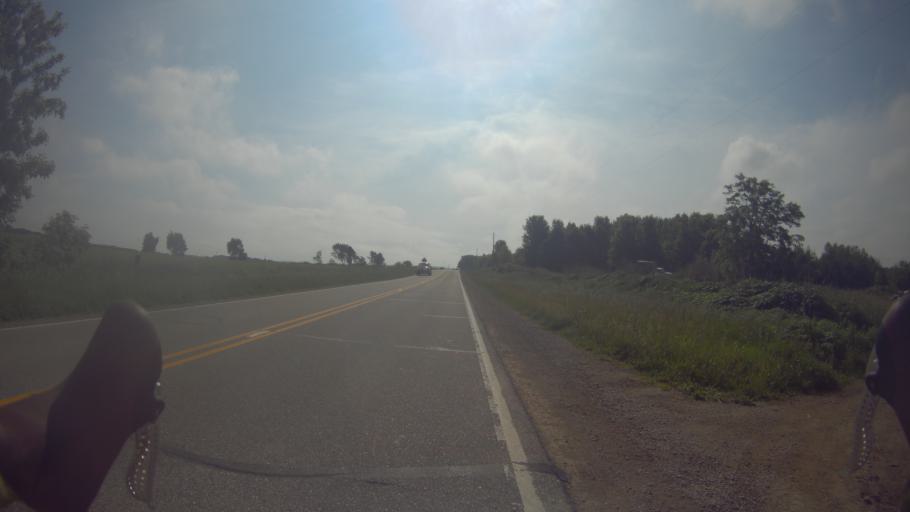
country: US
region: Wisconsin
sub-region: Dane County
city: McFarland
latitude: 43.0148
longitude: -89.2646
